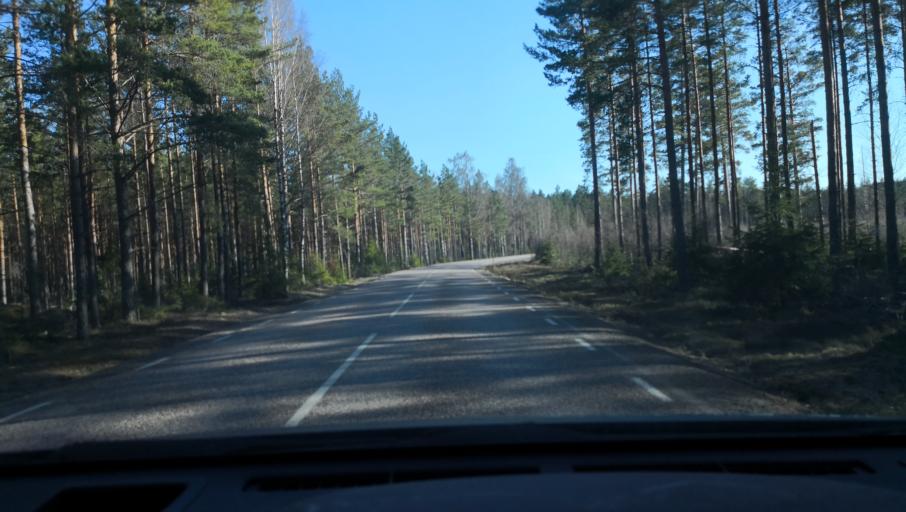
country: SE
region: Dalarna
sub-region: Avesta Kommun
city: Avesta
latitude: 59.9812
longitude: 16.3366
